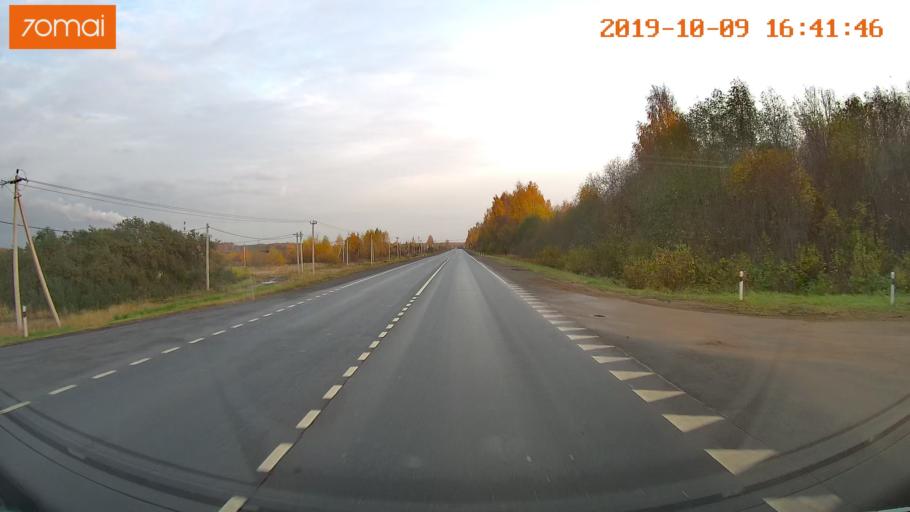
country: RU
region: Kostroma
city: Volgorechensk
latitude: 57.4696
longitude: 41.0872
